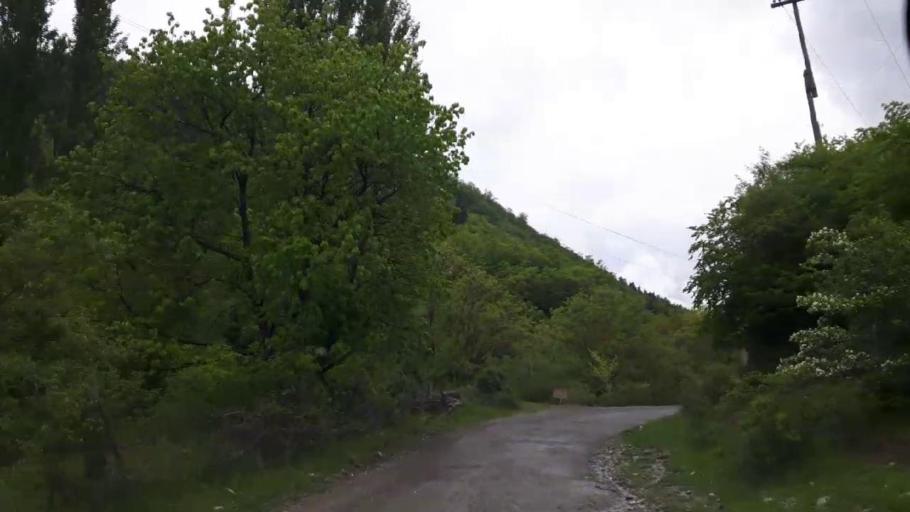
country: GE
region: Shida Kartli
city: Gori
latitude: 41.8837
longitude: 43.9979
